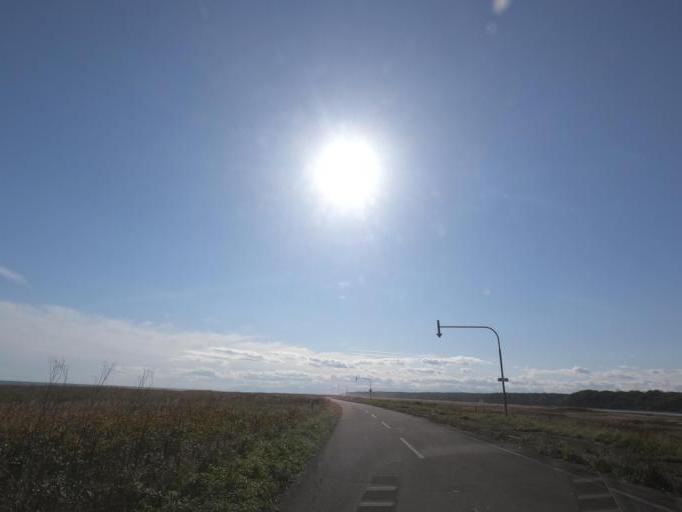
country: JP
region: Hokkaido
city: Obihiro
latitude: 42.5962
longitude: 143.5460
